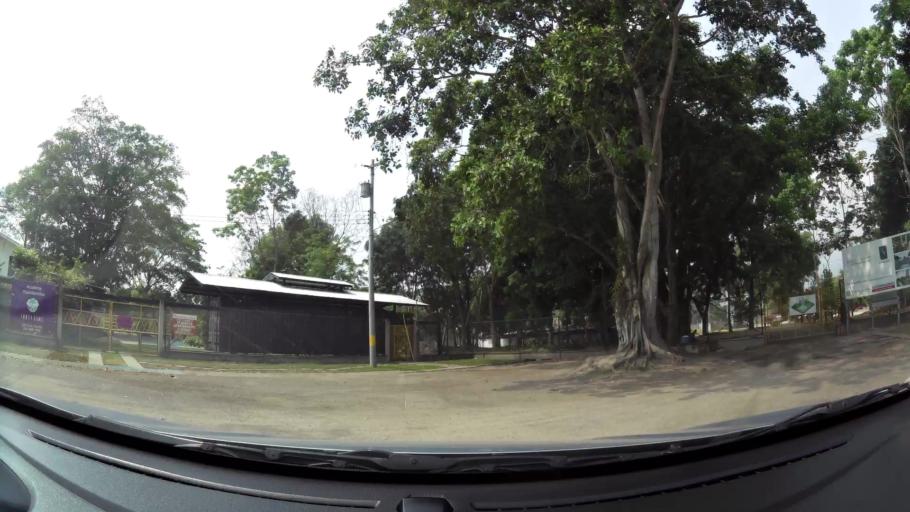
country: HN
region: Cortes
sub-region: San Pedro Sula
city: Pena Blanca
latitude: 15.5547
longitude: -88.0210
